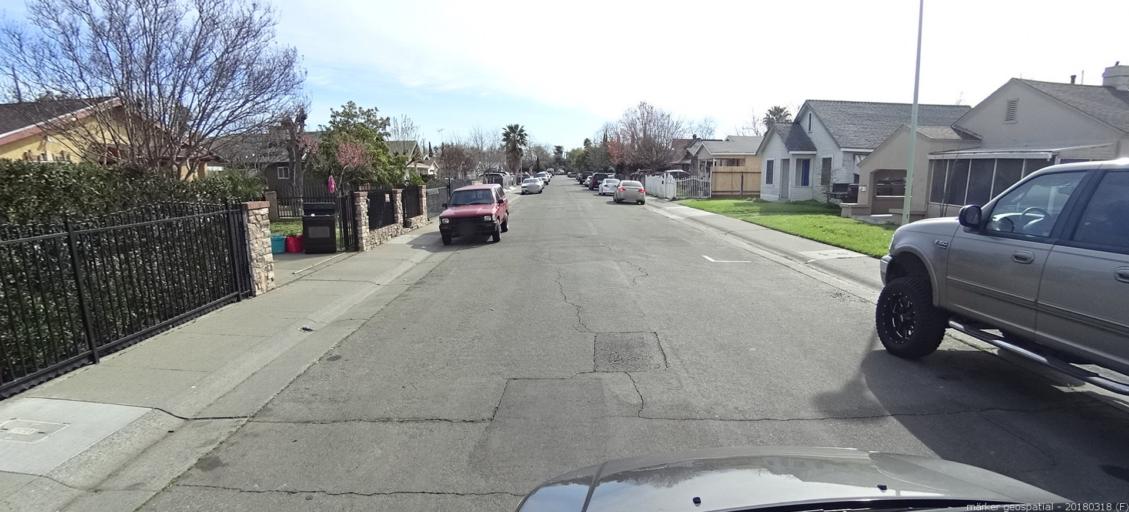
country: US
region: California
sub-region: Sacramento County
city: Parkway
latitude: 38.5327
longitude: -121.4676
